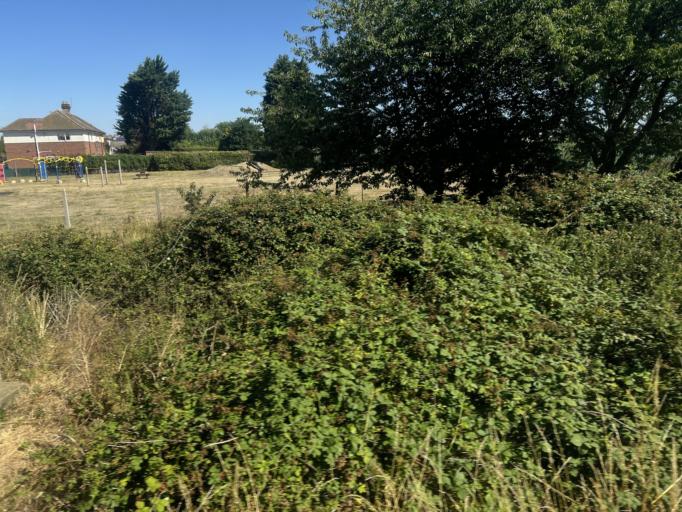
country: GB
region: England
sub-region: Lincolnshire
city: Sleaford
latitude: 52.9907
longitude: -0.3638
